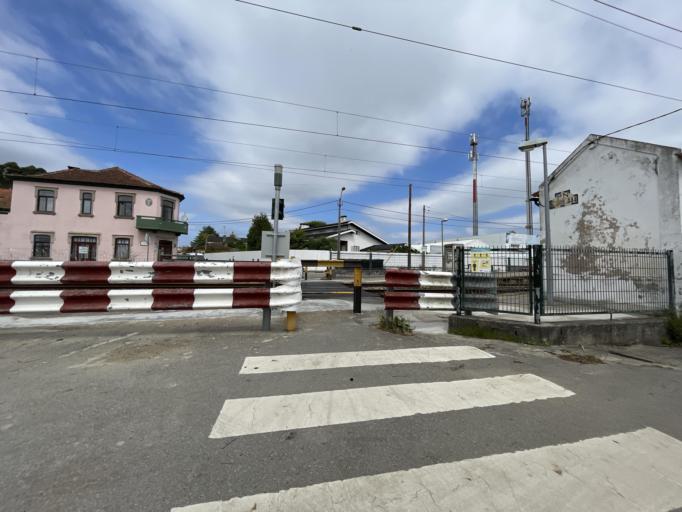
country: PT
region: Aveiro
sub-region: Ovar
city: Cortegaca
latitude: 40.9413
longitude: -8.6306
